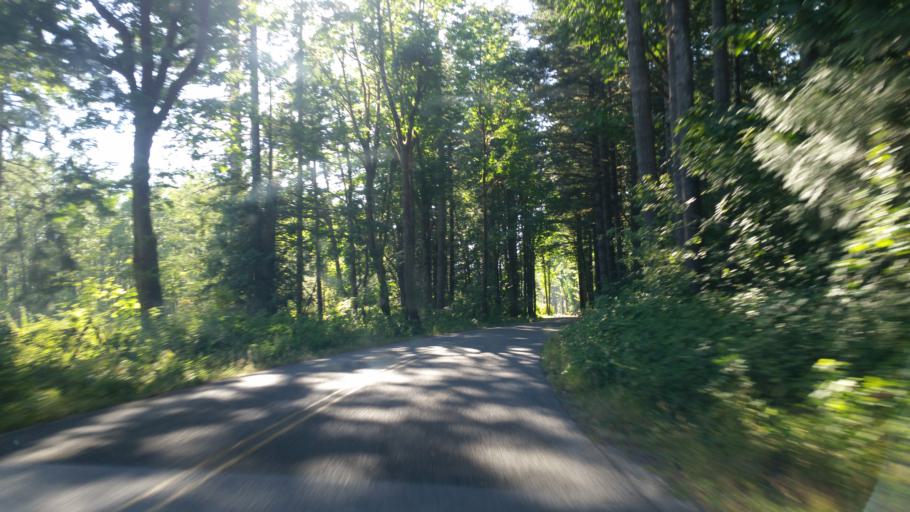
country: US
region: Washington
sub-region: Snohomish County
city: Gold Bar
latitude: 47.8417
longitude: -121.6408
